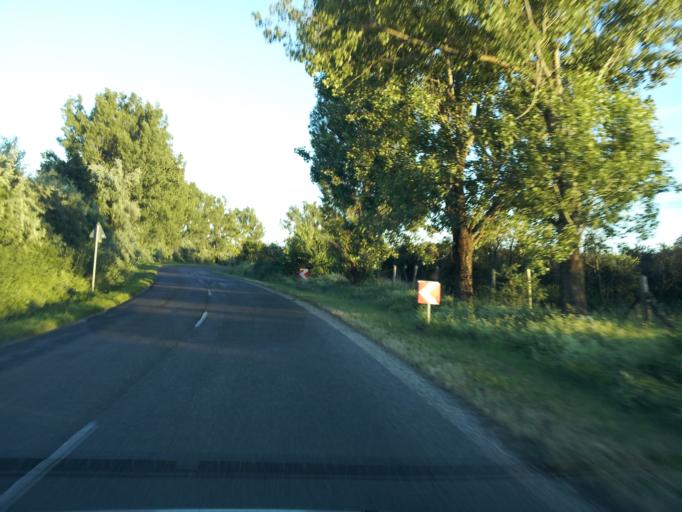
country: HU
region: Veszprem
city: Szentkiralyszabadja
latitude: 47.0451
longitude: 17.9304
